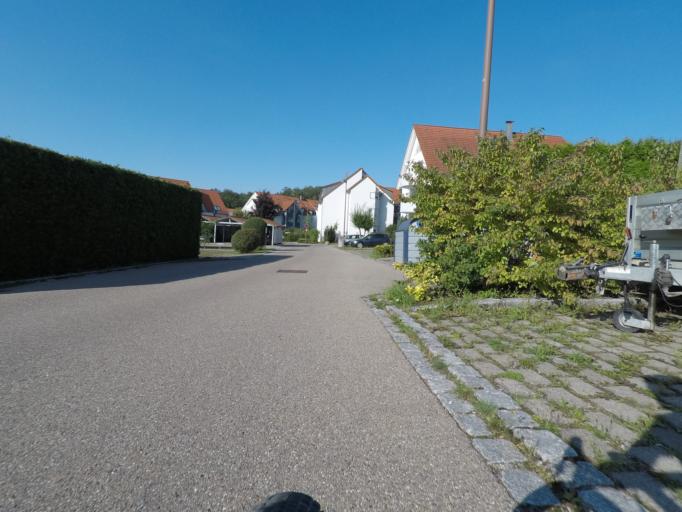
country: DE
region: Baden-Wuerttemberg
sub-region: Regierungsbezirk Stuttgart
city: Ehningen
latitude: 48.6623
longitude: 8.9583
